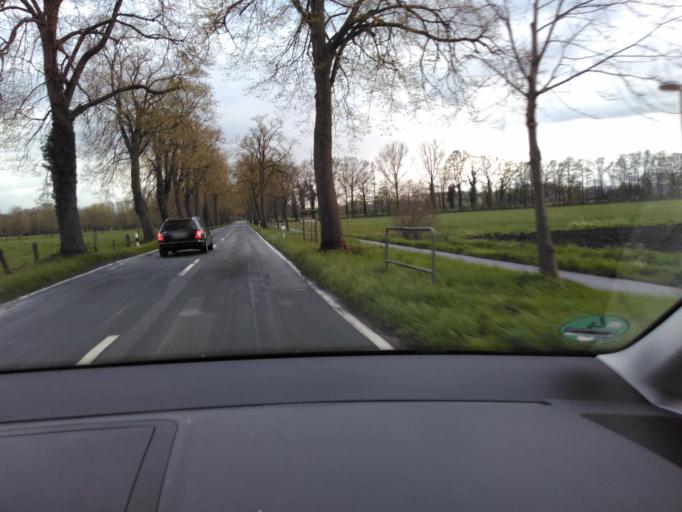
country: DE
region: North Rhine-Westphalia
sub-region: Regierungsbezirk Detmold
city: Verl
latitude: 51.9191
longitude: 8.4878
